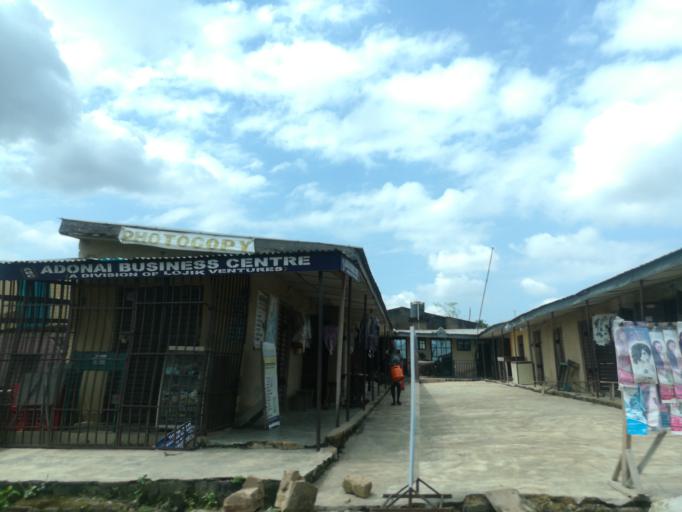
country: NG
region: Oyo
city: Egbeda
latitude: 7.4159
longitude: 4.0034
